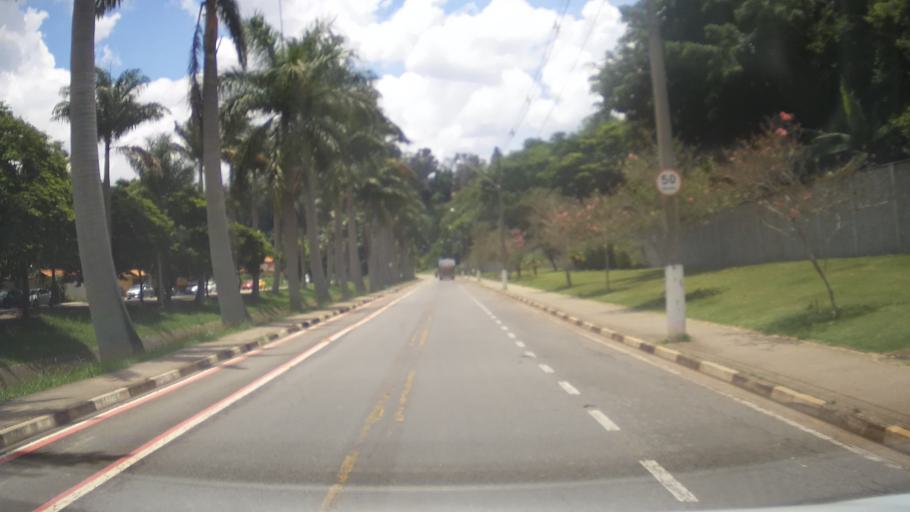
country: BR
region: Sao Paulo
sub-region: Vinhedo
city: Vinhedo
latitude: -23.0294
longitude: -46.9698
